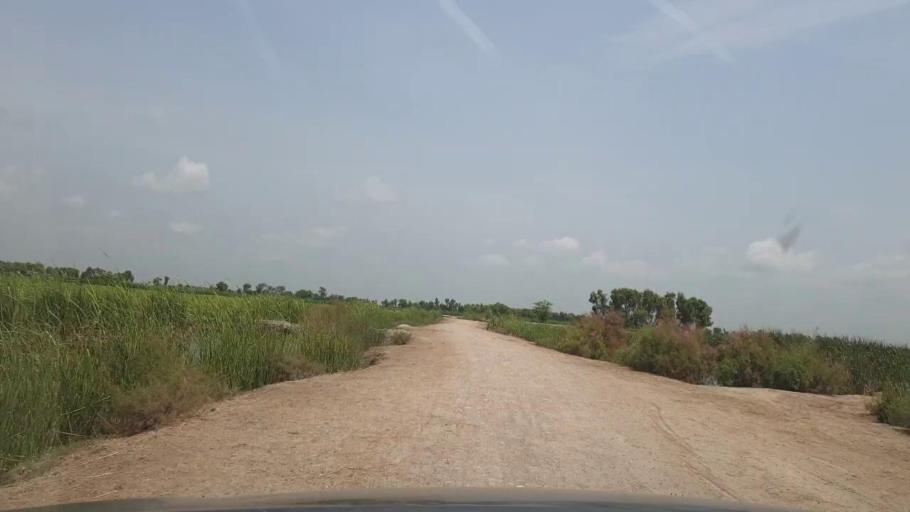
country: PK
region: Sindh
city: Ratodero
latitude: 27.9174
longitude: 68.2982
